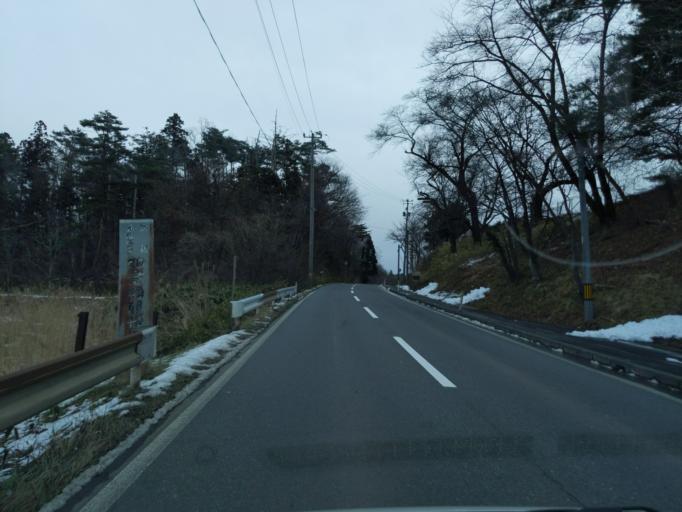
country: JP
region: Iwate
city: Mizusawa
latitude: 39.1554
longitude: 141.2104
